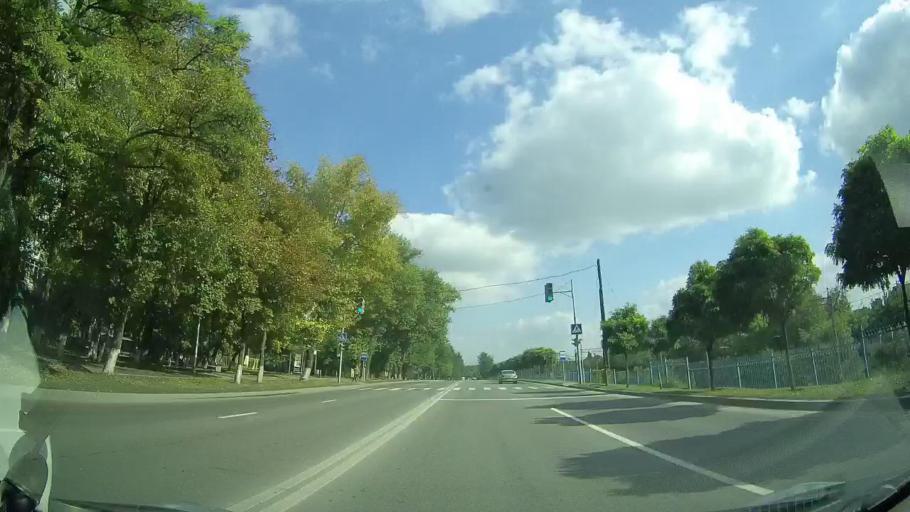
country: RU
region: Rostov
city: Imeni Chkalova
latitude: 47.2616
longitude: 39.7826
